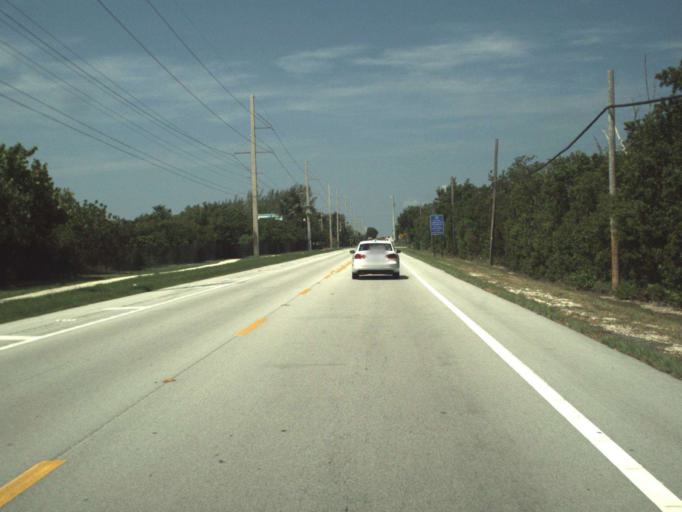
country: US
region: Florida
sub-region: Monroe County
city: Islamorada
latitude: 24.8069
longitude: -80.8398
